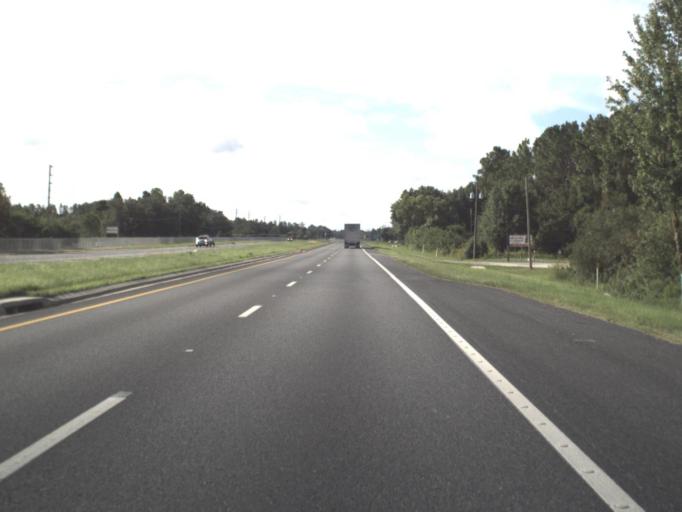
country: US
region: Florida
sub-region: Pasco County
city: Land O' Lakes
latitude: 28.2696
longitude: -82.4801
